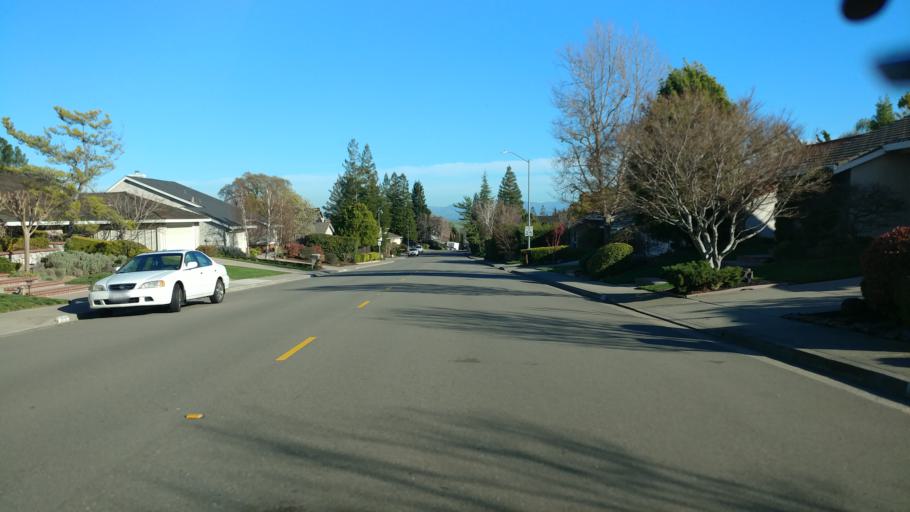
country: US
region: California
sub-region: Contra Costa County
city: San Ramon
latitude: 37.7557
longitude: -121.9711
